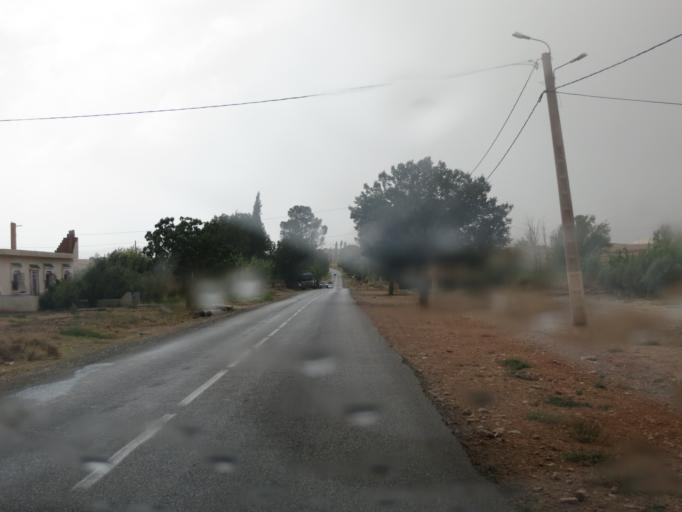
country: MA
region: Meknes-Tafilalet
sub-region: Khenifra
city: Itzer
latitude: 32.8786
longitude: -4.9484
